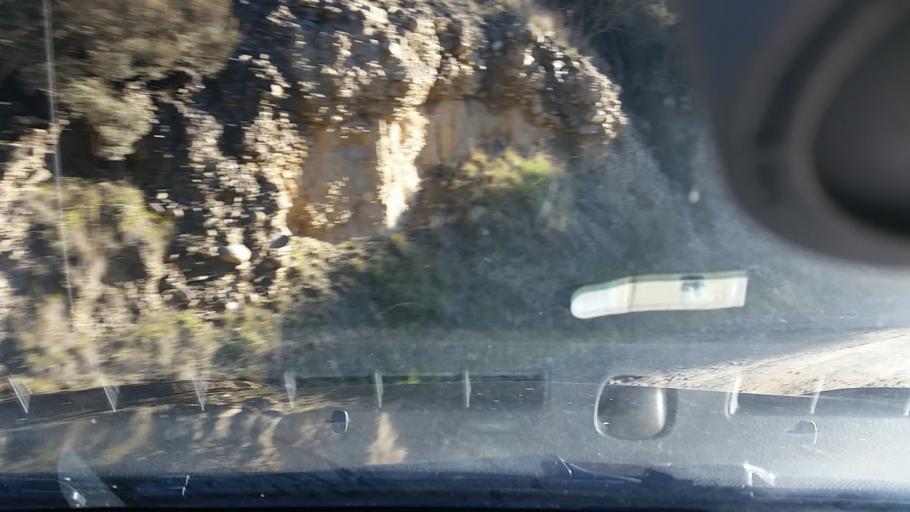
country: NZ
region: Marlborough
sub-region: Marlborough District
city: Blenheim
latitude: -41.5869
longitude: 174.0712
